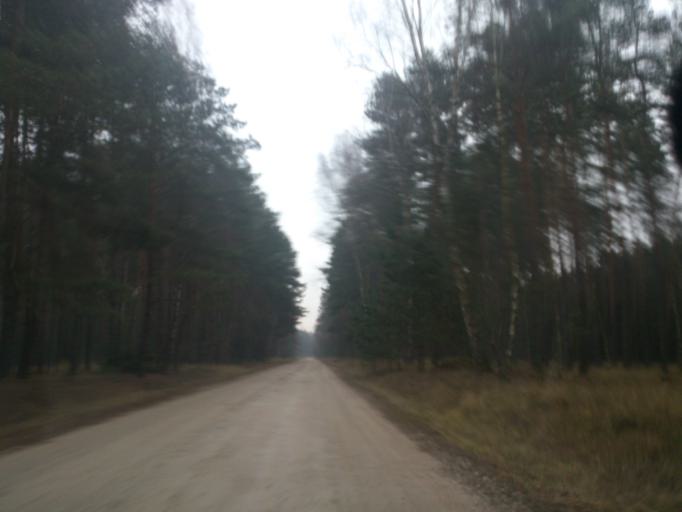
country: PL
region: Kujawsko-Pomorskie
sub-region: Powiat golubsko-dobrzynski
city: Radomin
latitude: 53.1785
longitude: 19.1878
